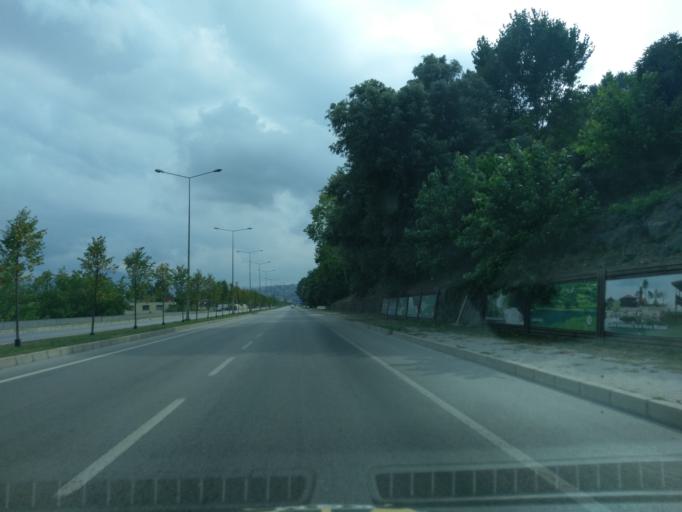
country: TR
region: Samsun
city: Samsun
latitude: 41.3053
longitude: 36.2975
